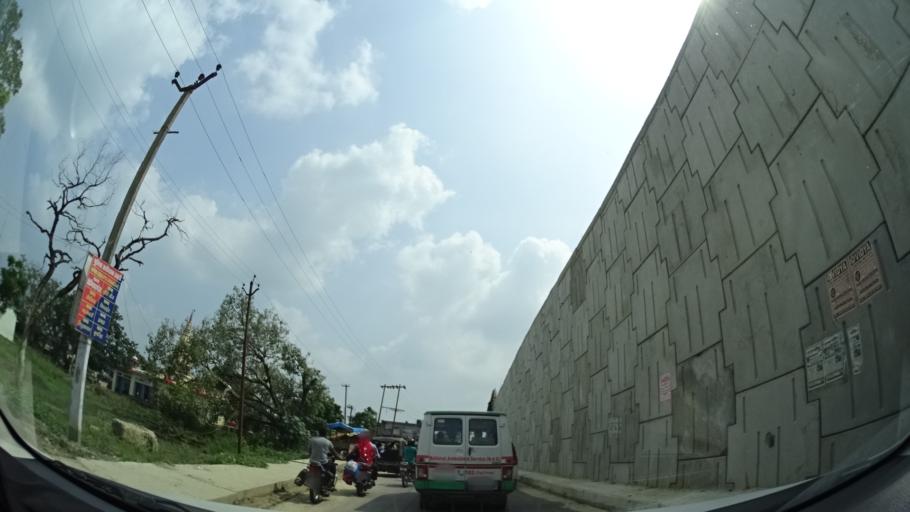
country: IN
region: Uttar Pradesh
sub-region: Maharajganj
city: Anandnagar
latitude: 27.0304
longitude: 83.2699
